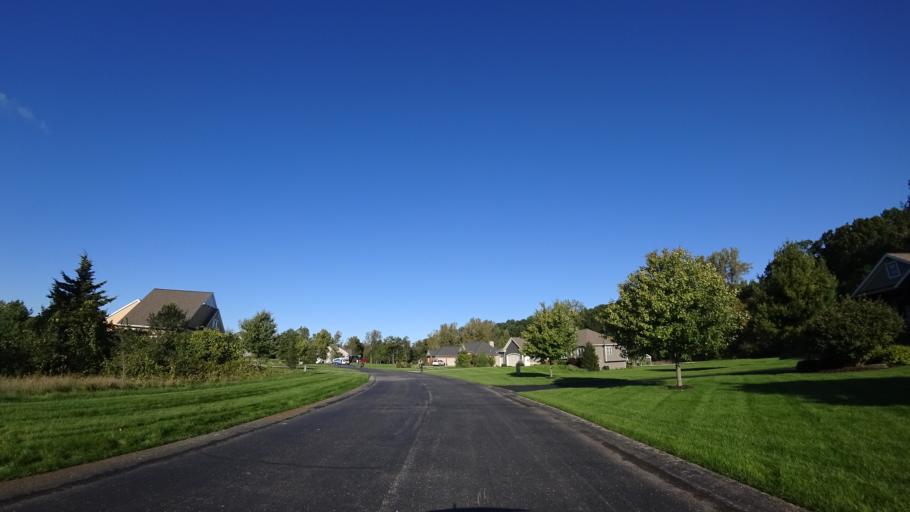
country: US
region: Michigan
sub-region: Kent County
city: Grandville
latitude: 42.9376
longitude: -85.7630
